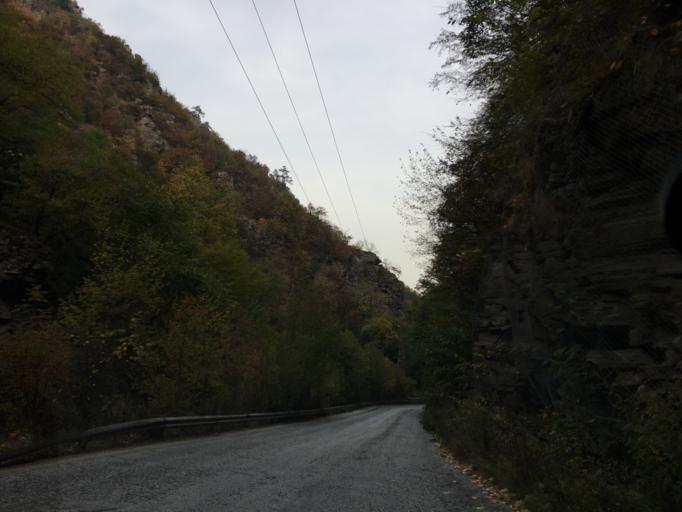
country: BG
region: Pazardzhik
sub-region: Obshtina Belovo
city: Belovo
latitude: 42.1634
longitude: 23.9695
